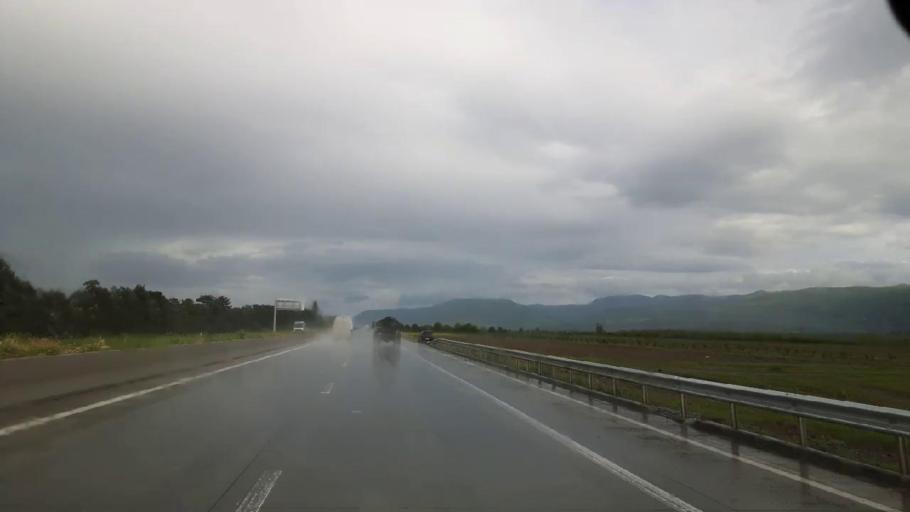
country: GE
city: Agara
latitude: 42.0417
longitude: 43.9277
